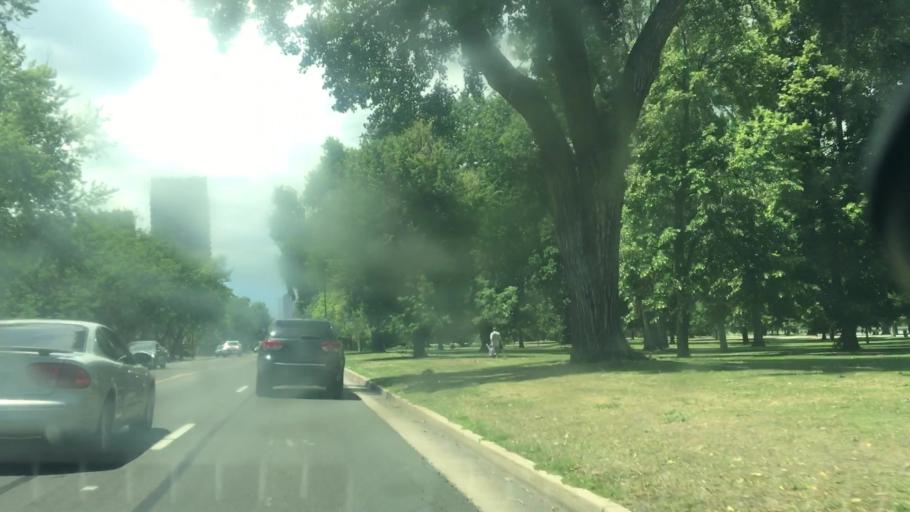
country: US
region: Colorado
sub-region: Denver County
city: Denver
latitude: 39.7438
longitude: -104.9471
